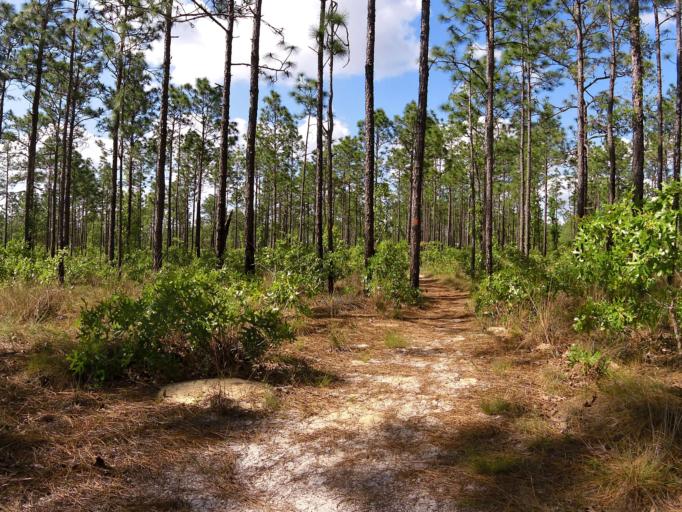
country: US
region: Florida
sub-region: Clay County
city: Keystone Heights
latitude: 29.8407
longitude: -81.9479
